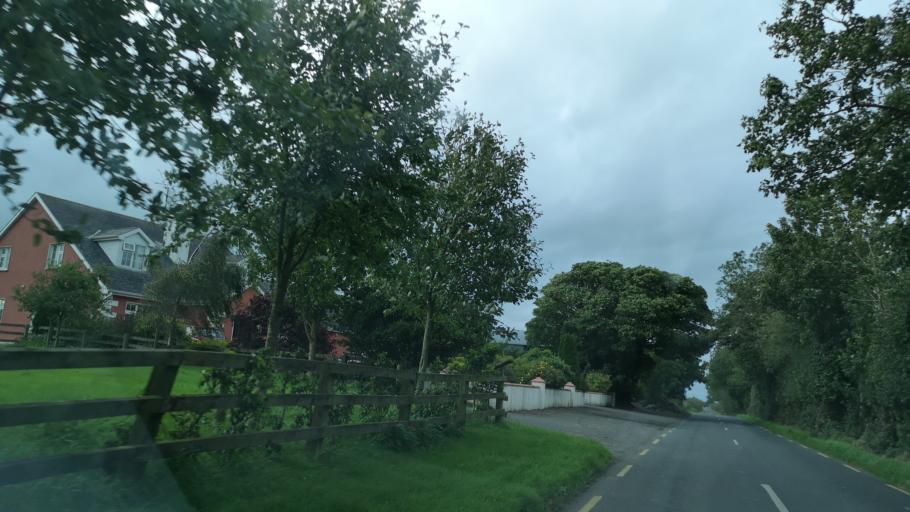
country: IE
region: Leinster
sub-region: Uibh Fhaili
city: Ferbane
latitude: 53.2022
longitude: -7.7829
